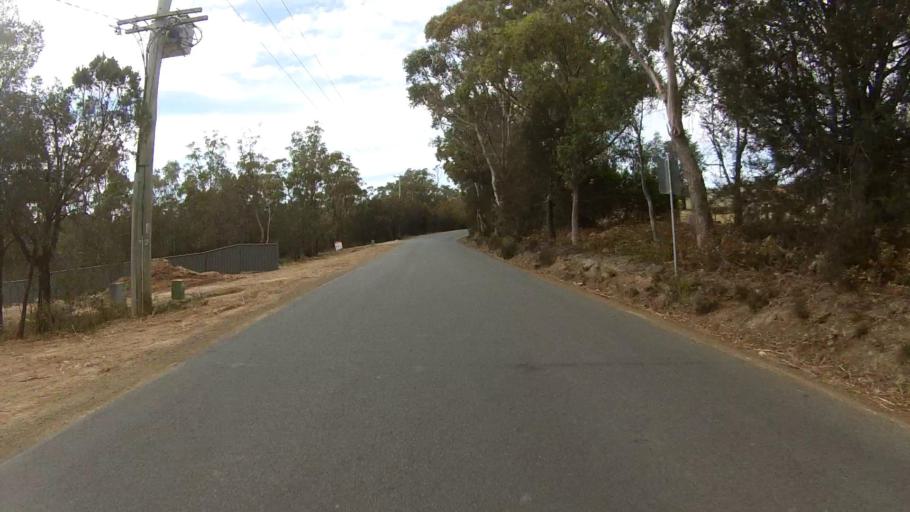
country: AU
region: Tasmania
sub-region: Kingborough
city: Blackmans Bay
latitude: -43.0240
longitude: 147.2986
